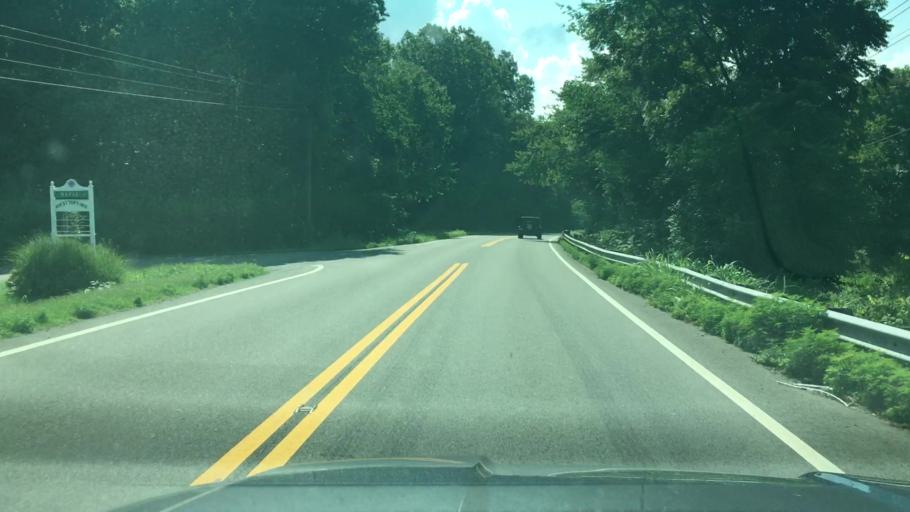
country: US
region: Tennessee
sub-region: Williamson County
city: Nolensville
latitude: 35.8713
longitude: -86.7260
